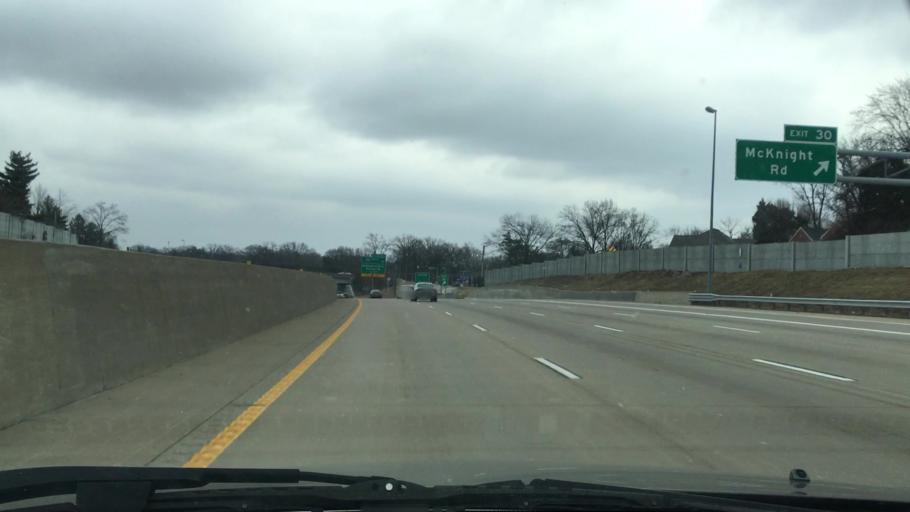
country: US
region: Missouri
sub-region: Saint Louis County
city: Brentwood
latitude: 38.6302
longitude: -90.3658
